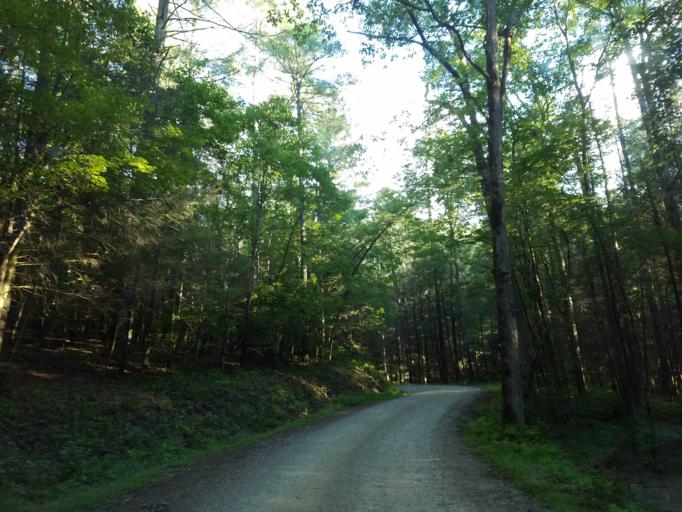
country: US
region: Georgia
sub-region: Union County
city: Blairsville
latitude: 34.7550
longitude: -84.0675
